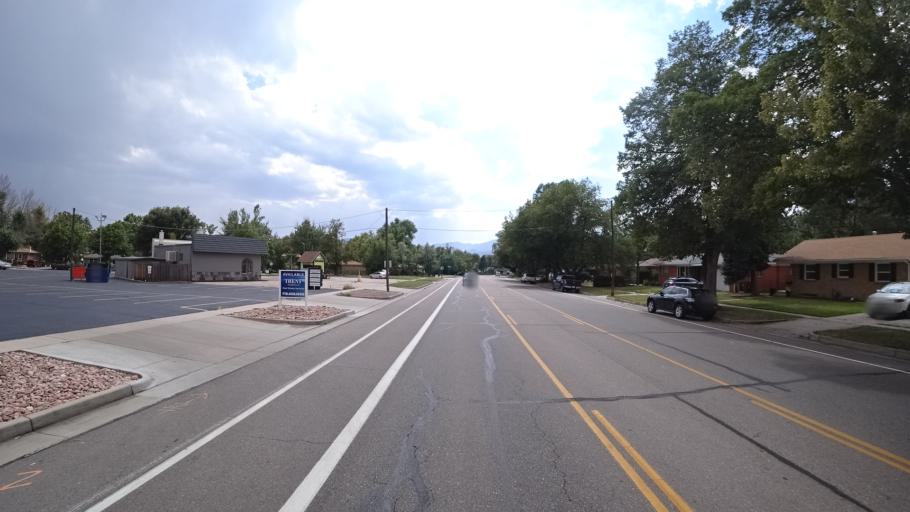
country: US
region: Colorado
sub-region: El Paso County
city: Colorado Springs
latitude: 38.8636
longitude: -104.8102
